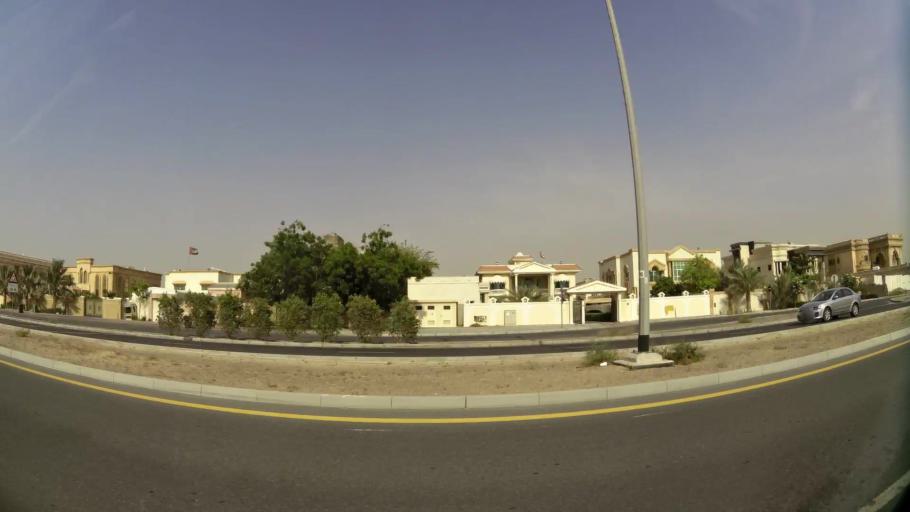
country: AE
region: Ash Shariqah
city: Sharjah
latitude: 25.2558
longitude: 55.4554
